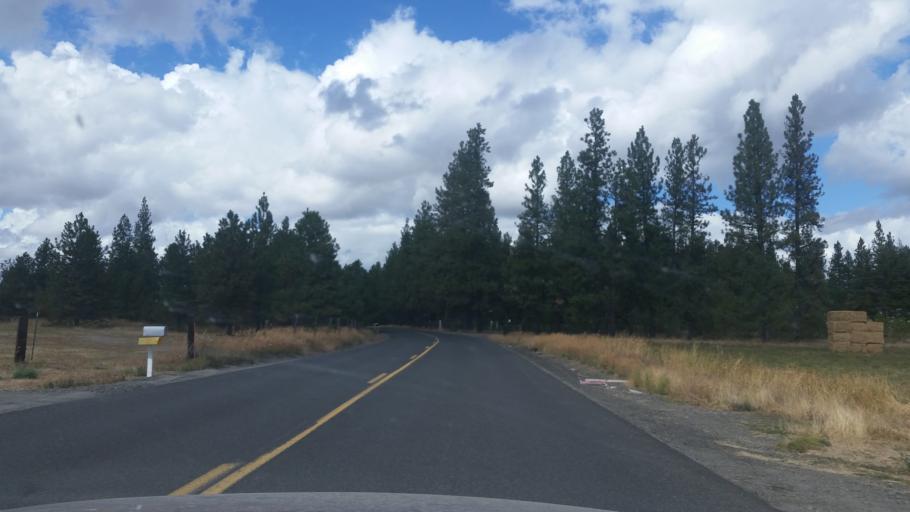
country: US
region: Washington
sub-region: Spokane County
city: Cheney
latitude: 47.5429
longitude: -117.4782
